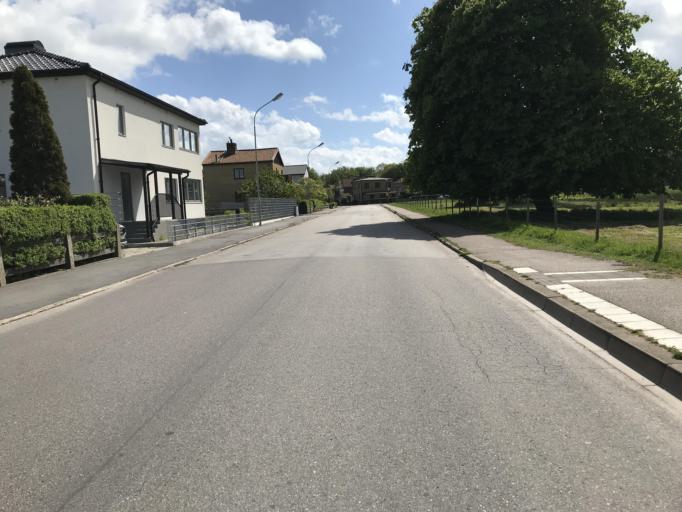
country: SE
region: Skane
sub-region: Landskrona
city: Landskrona
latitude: 55.8808
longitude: 12.8216
